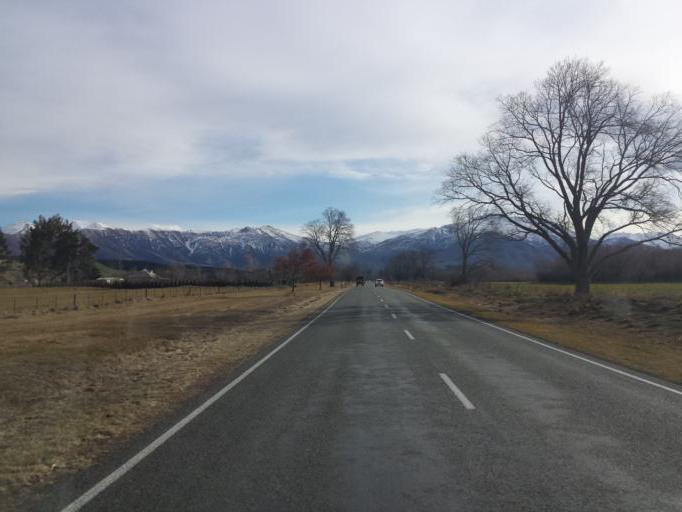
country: NZ
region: Canterbury
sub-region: Timaru District
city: Pleasant Point
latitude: -44.0585
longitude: 170.7748
